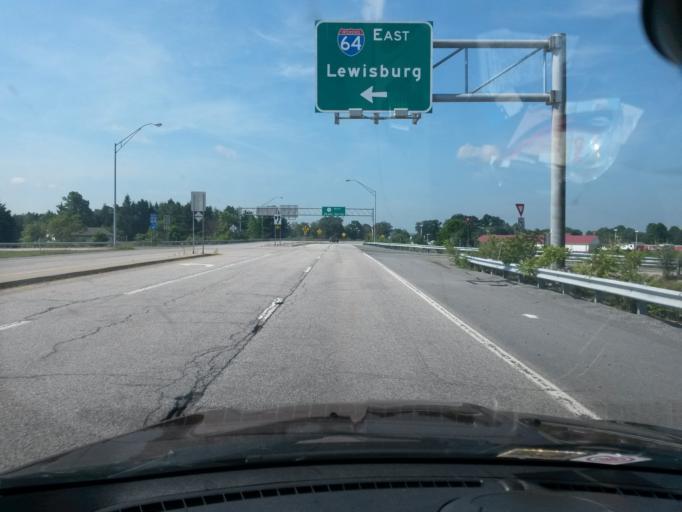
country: US
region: West Virginia
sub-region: Raleigh County
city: Daniels
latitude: 37.7725
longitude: -81.0665
